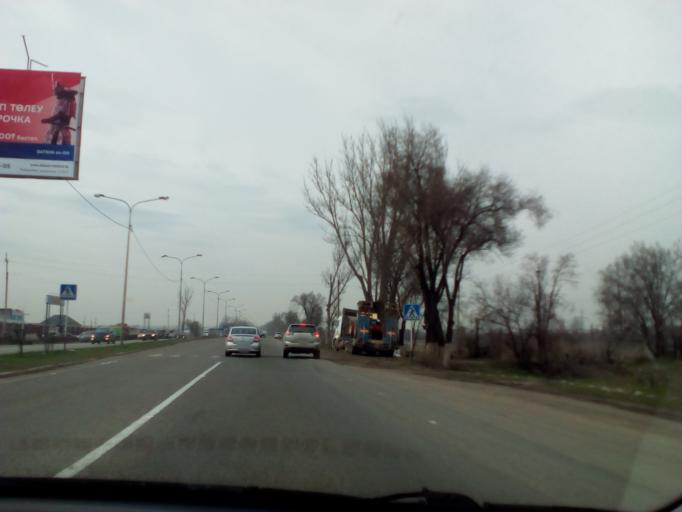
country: KZ
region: Almaty Oblysy
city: Burunday
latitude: 43.2208
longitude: 76.6295
